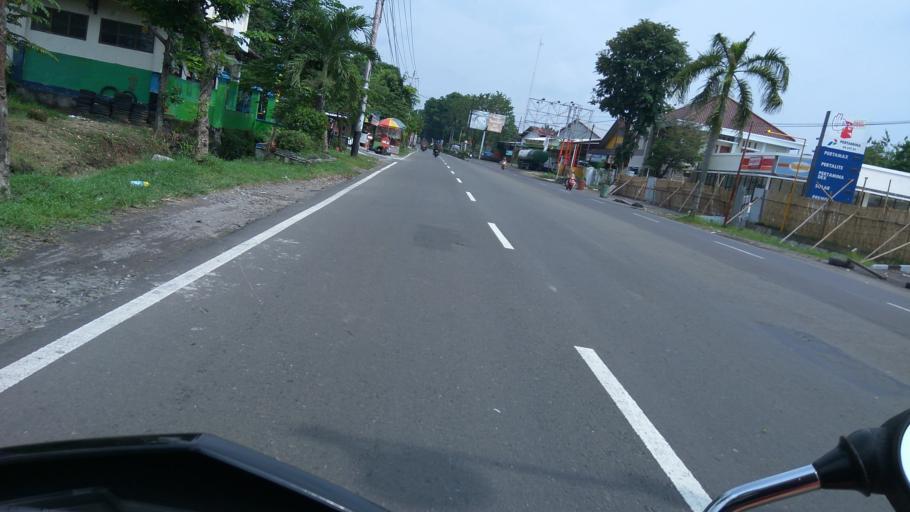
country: ID
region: Central Java
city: Jaten
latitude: -7.5869
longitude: 110.9200
